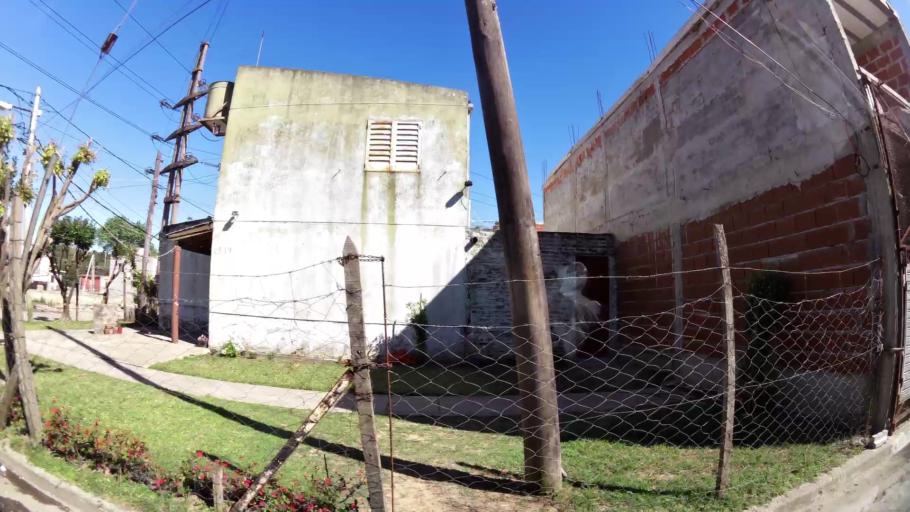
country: AR
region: Buenos Aires
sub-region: Partido de Quilmes
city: Quilmes
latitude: -34.7033
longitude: -58.3030
